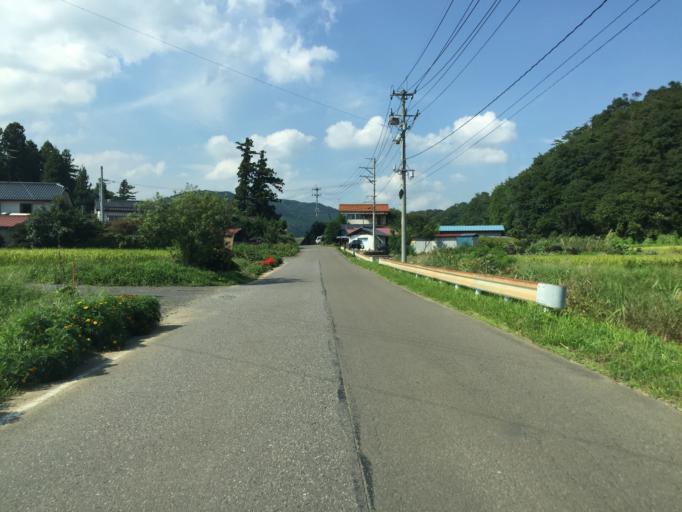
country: JP
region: Fukushima
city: Nihommatsu
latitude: 37.5890
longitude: 140.3892
